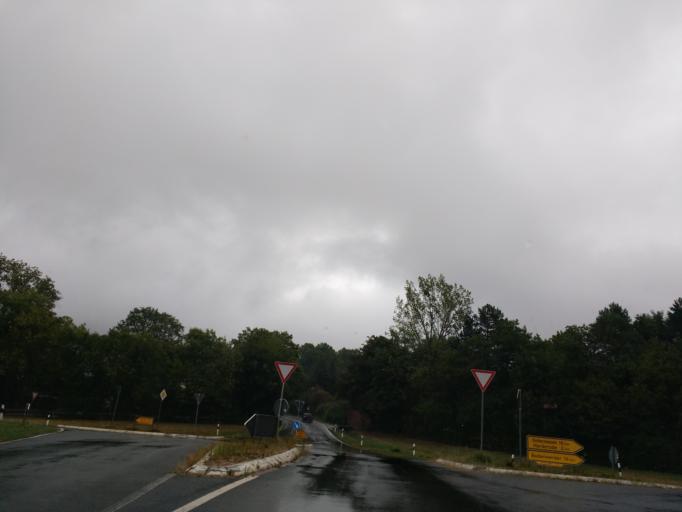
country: DE
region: Lower Saxony
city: Heyen
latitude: 52.0612
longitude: 9.5240
